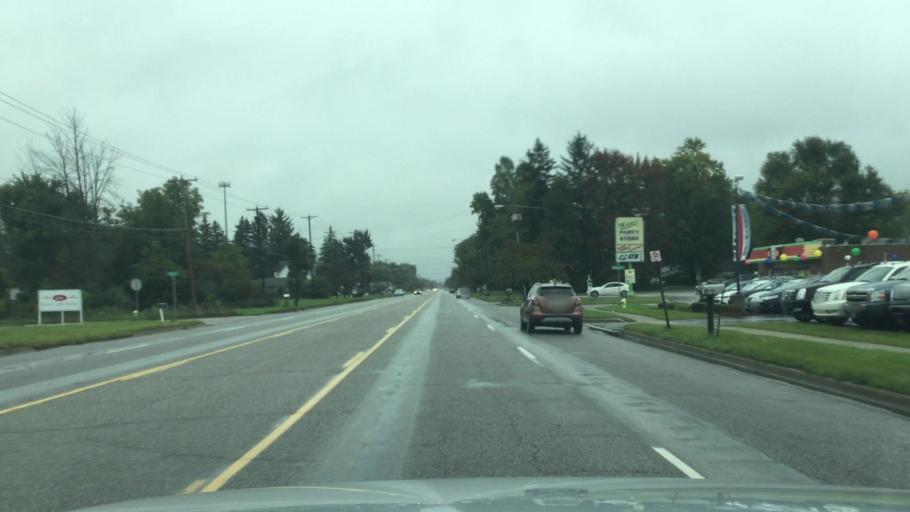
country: US
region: Michigan
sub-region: Saginaw County
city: Buena Vista
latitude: 43.3890
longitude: -83.9041
